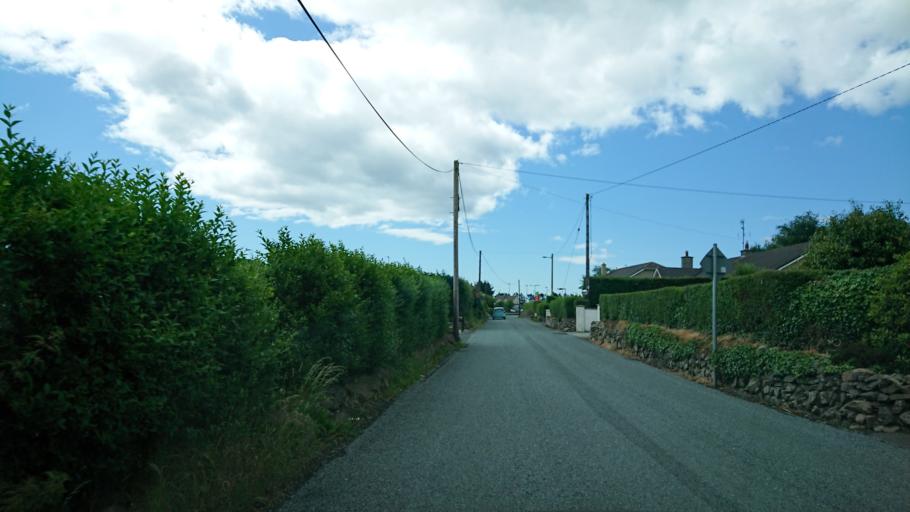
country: IE
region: Munster
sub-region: Waterford
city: Tra Mhor
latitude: 52.1745
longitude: -7.1404
